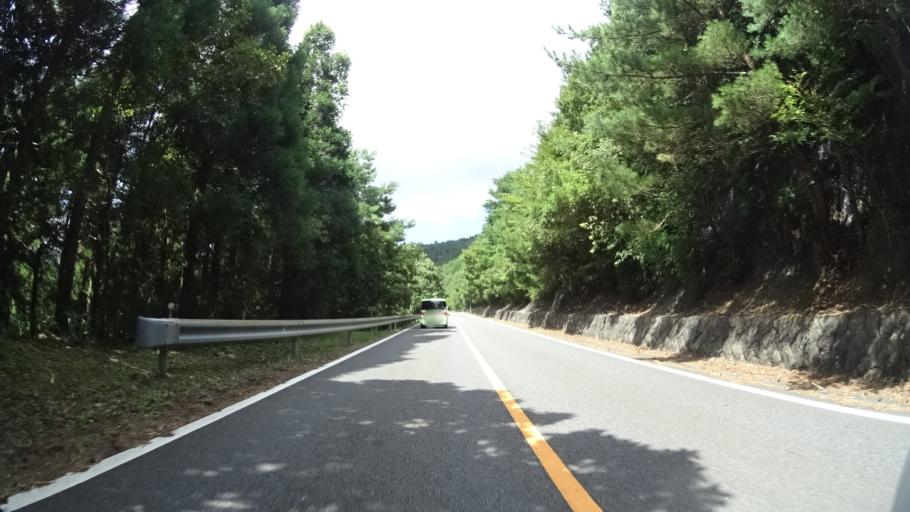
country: JP
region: Oita
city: Tsukawaki
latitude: 33.2060
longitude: 131.2945
